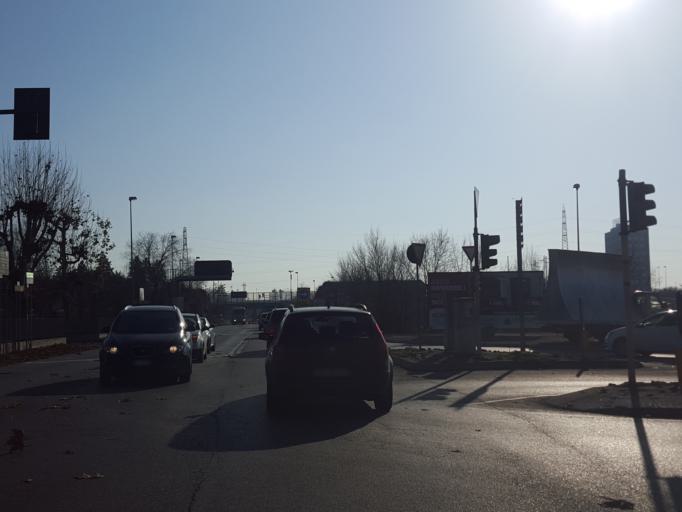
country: IT
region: Veneto
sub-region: Provincia di Verona
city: Verona
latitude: 45.4015
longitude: 10.9911
